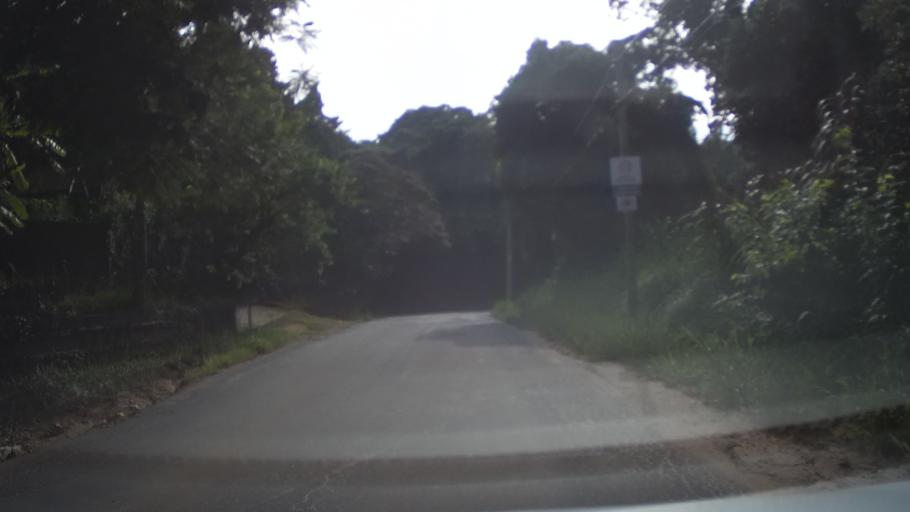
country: BR
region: Sao Paulo
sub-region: Itupeva
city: Itupeva
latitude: -23.2104
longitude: -47.0677
